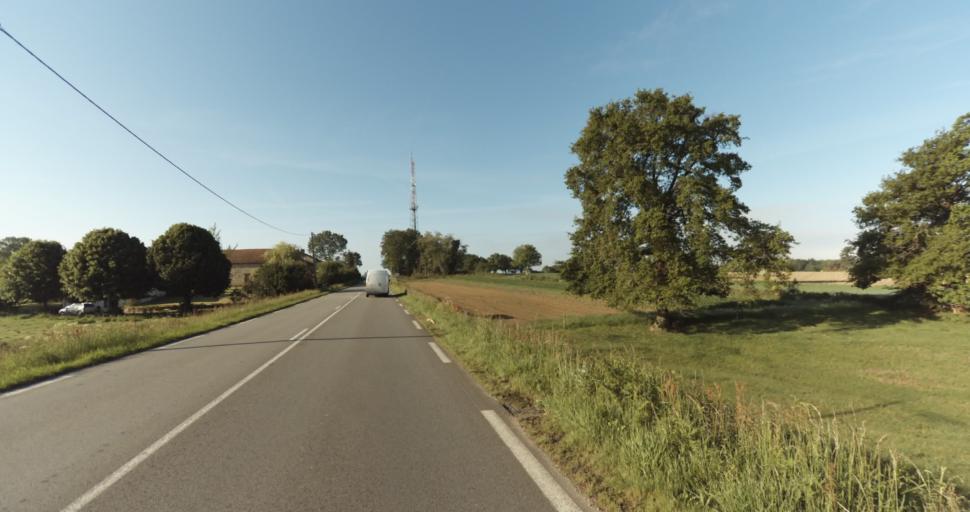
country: FR
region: Limousin
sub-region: Departement de la Haute-Vienne
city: Condat-sur-Vienne
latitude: 45.7798
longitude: 1.2881
